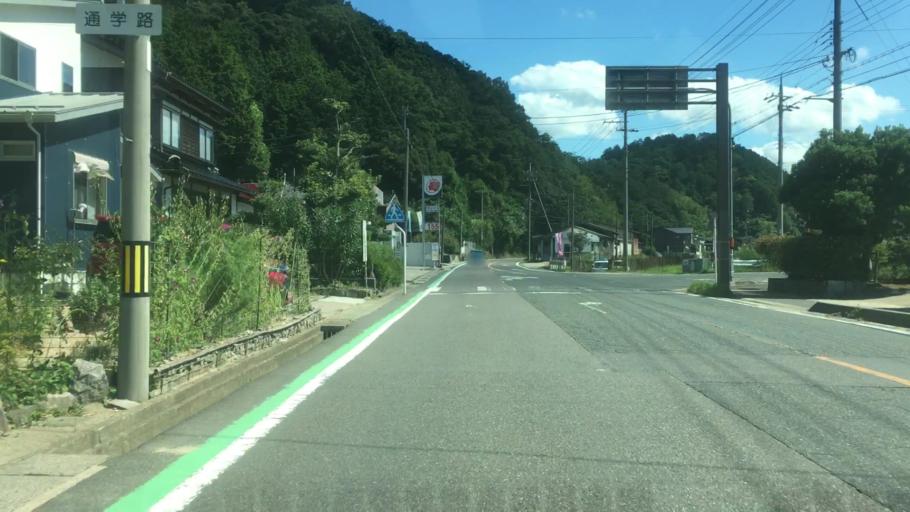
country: JP
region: Hyogo
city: Toyooka
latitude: 35.6001
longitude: 134.9028
